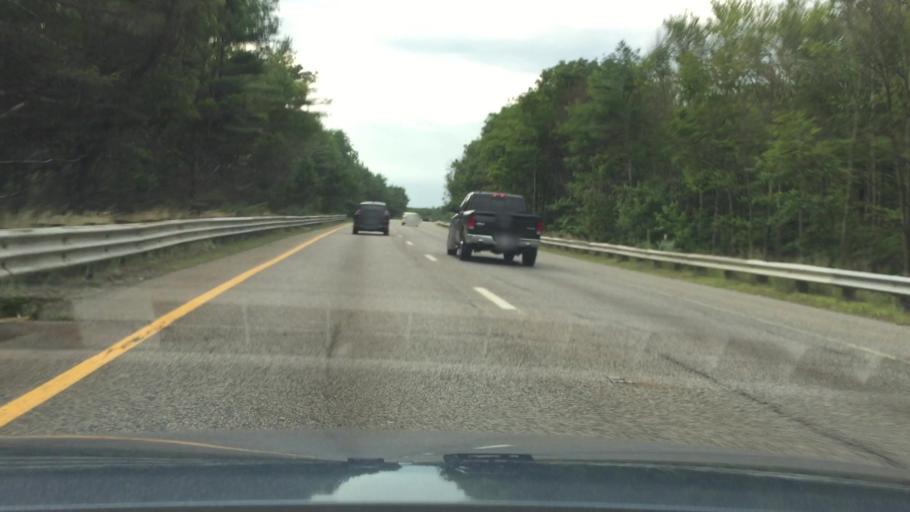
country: US
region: Massachusetts
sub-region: Plymouth County
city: Rockland
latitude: 42.1706
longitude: -70.9044
